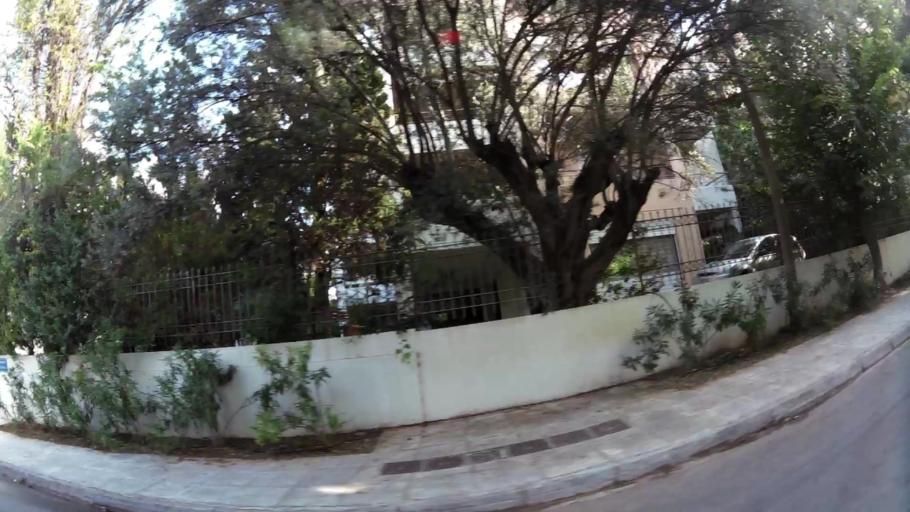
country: GR
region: Attica
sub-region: Nomarchia Athinas
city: Melissia
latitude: 38.0533
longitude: 23.8177
